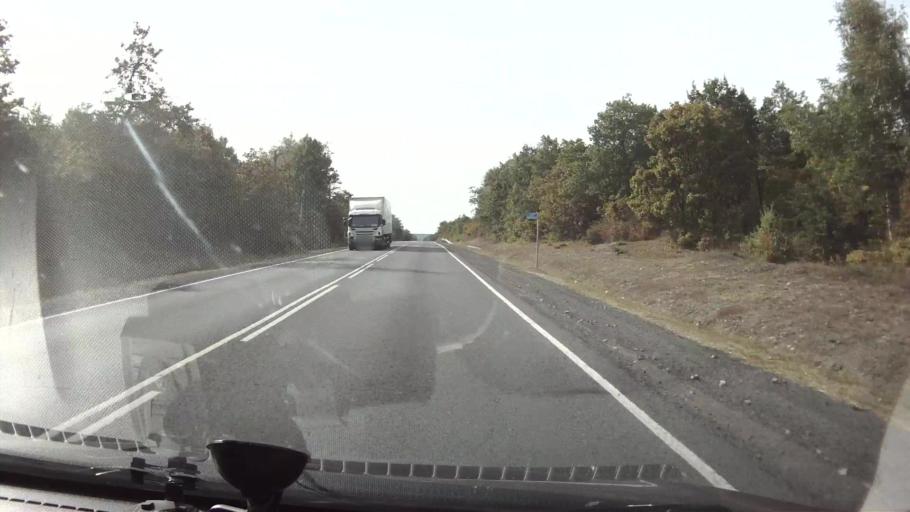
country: RU
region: Saratov
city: Vol'sk
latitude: 52.1100
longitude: 47.3621
